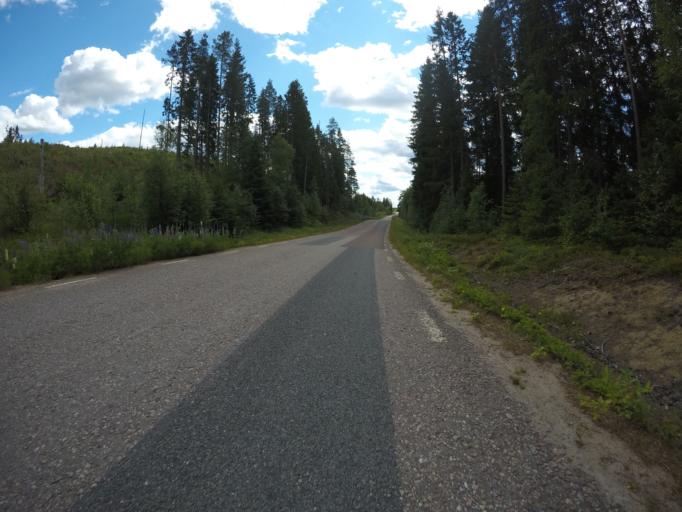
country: SE
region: OErebro
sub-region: Hallefors Kommun
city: Haellefors
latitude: 60.0670
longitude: 14.4936
